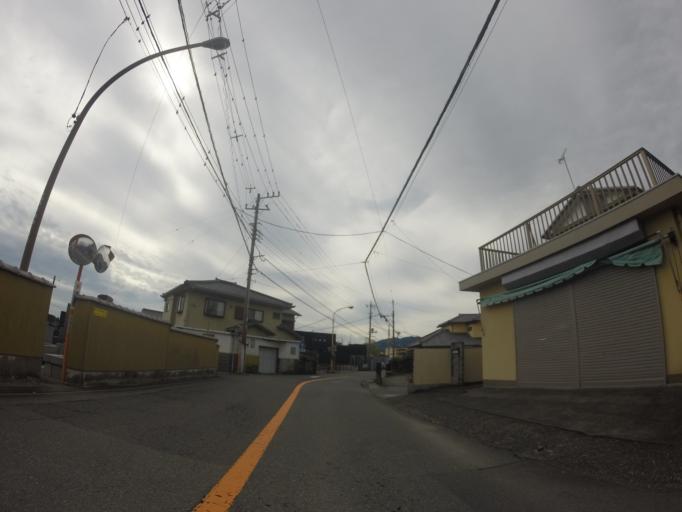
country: JP
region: Shizuoka
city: Fuji
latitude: 35.1924
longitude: 138.6517
